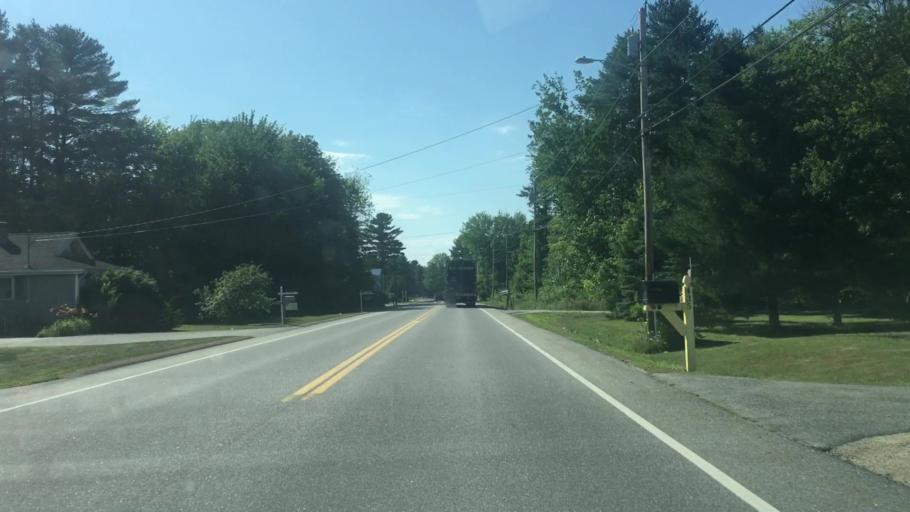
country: US
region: Maine
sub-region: York County
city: Buxton
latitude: 43.5688
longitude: -70.5074
